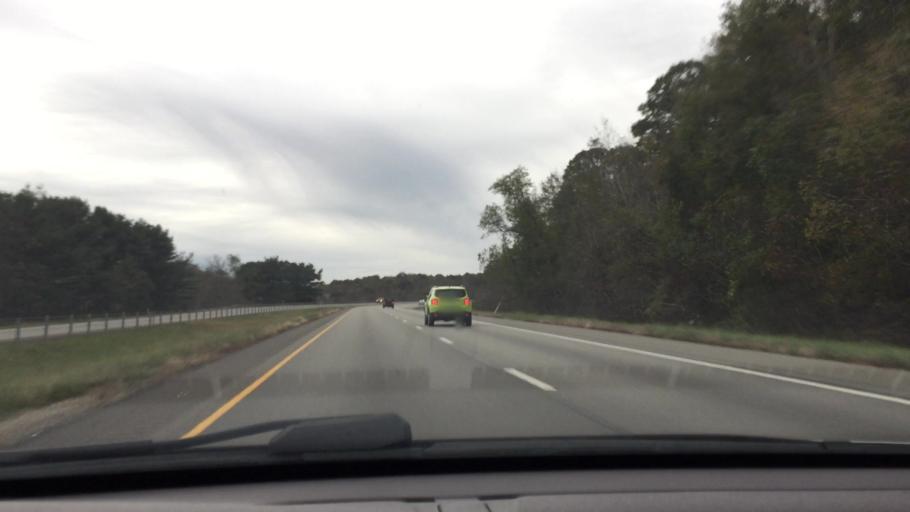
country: US
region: Pennsylvania
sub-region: Beaver County
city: Beaver
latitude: 40.6885
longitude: -80.3485
